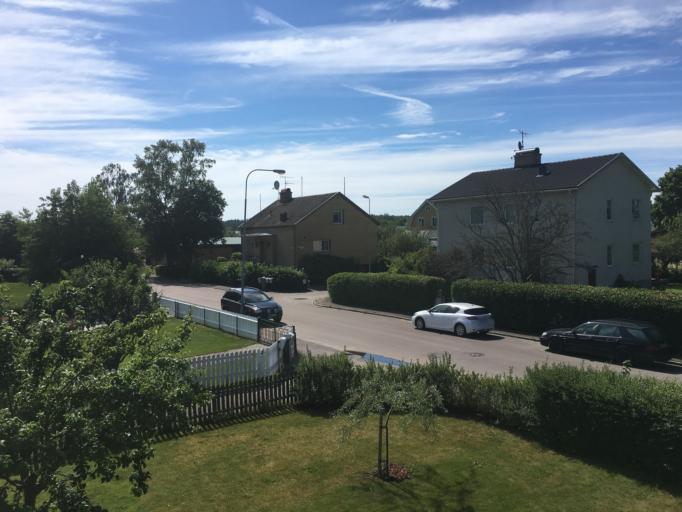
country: SE
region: Vaermland
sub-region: Karlstads Kommun
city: Karlstad
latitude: 59.3686
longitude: 13.4713
